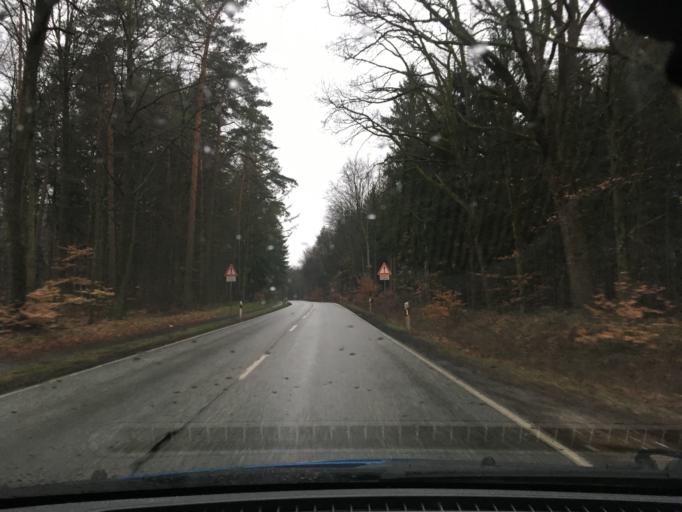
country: DE
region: Schleswig-Holstein
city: Krukow
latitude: 53.3946
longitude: 10.4755
